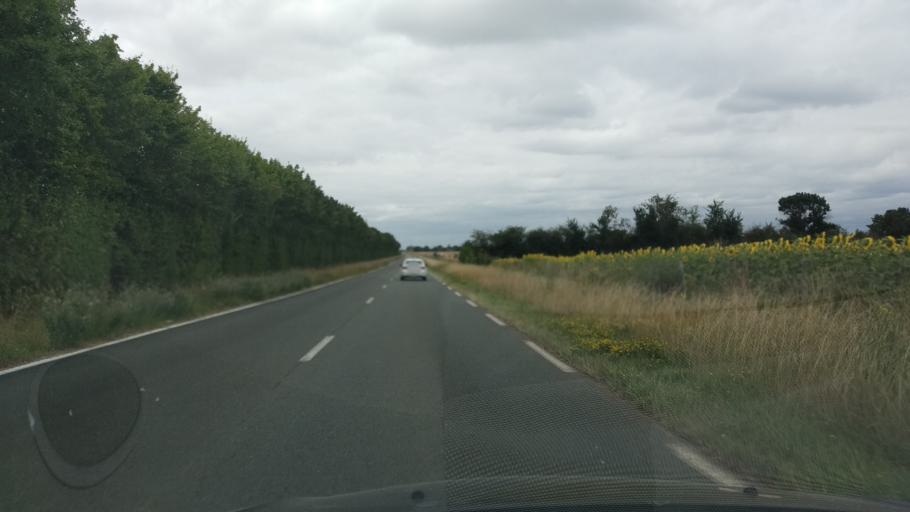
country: FR
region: Poitou-Charentes
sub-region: Departement de la Vienne
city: La Villedieu-du-Clain
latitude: 46.4203
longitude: 0.3828
